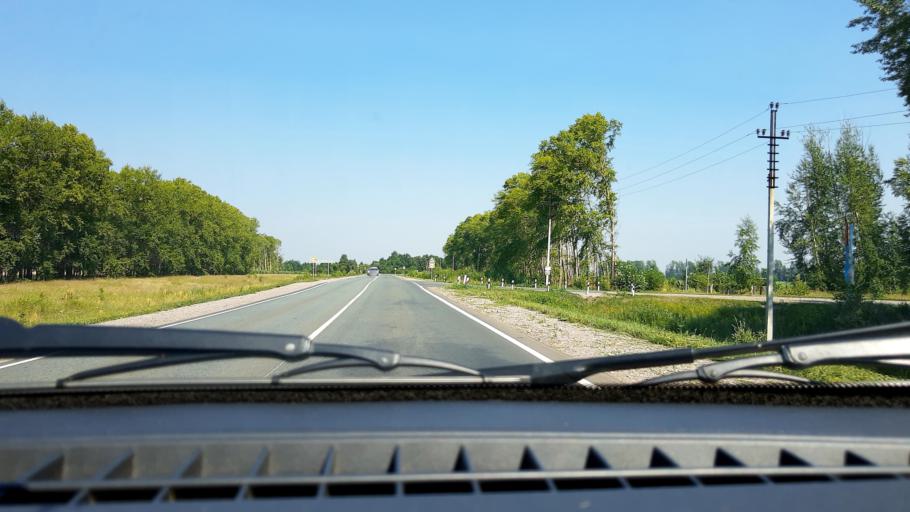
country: RU
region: Bashkortostan
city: Kushnarenkovo
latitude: 55.0602
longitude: 55.1866
